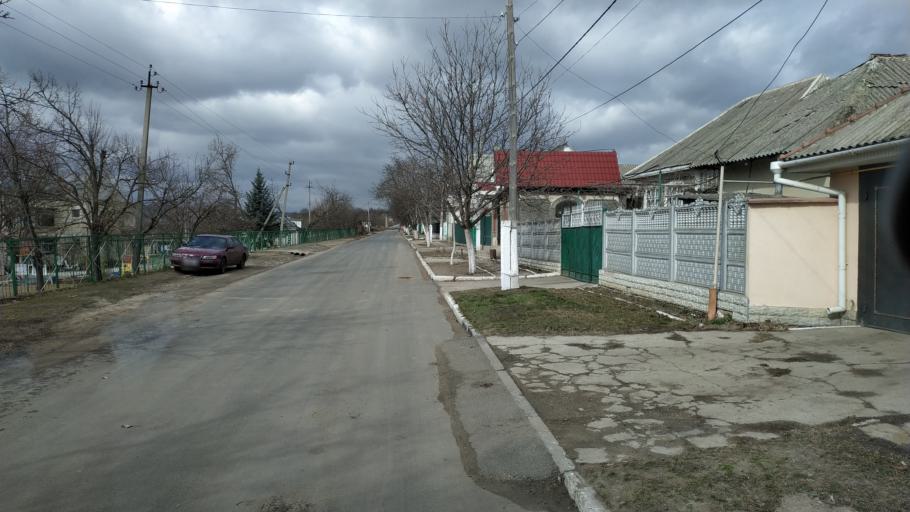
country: MD
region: Stinga Nistrului
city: Bucovat
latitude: 47.2232
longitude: 28.4391
